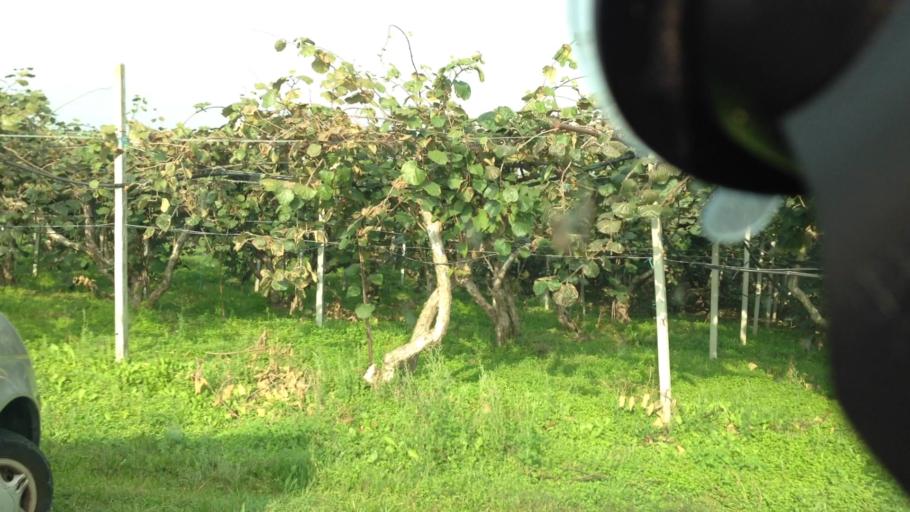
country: IT
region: Piedmont
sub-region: Provincia di Vercelli
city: Borgo d'Ale
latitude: 45.3416
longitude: 8.0663
